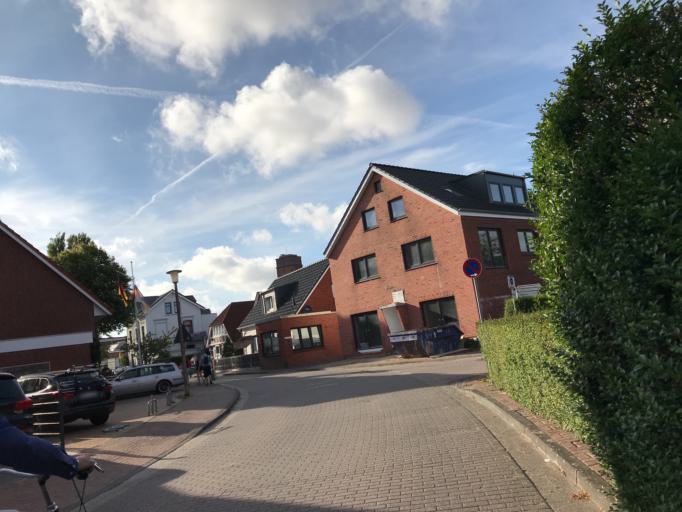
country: DE
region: Lower Saxony
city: Borkum
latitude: 53.5861
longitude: 6.6729
